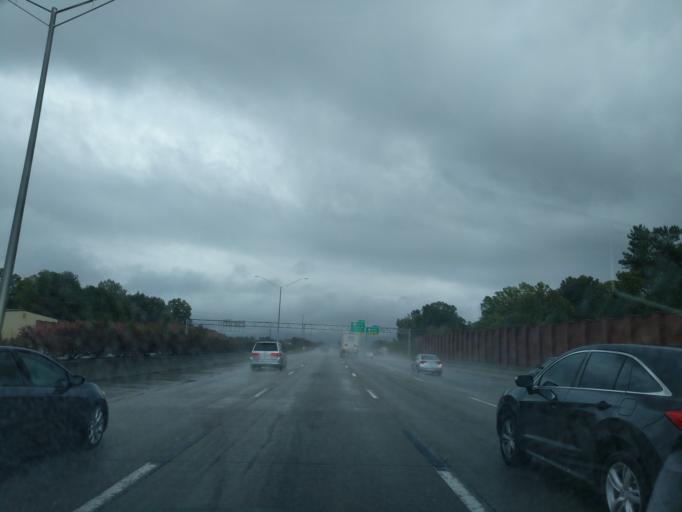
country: US
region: North Carolina
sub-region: Durham County
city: Durham
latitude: 36.0286
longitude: -78.9305
